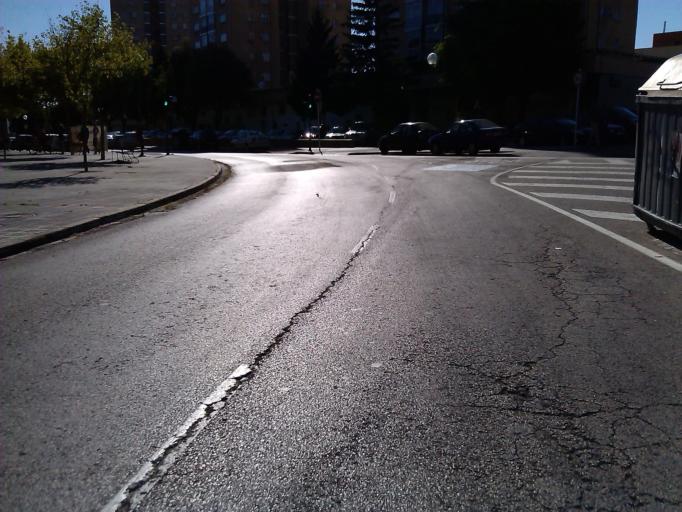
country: ES
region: Castille and Leon
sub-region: Provincia de Burgos
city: Burgos
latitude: 42.3538
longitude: -3.6724
